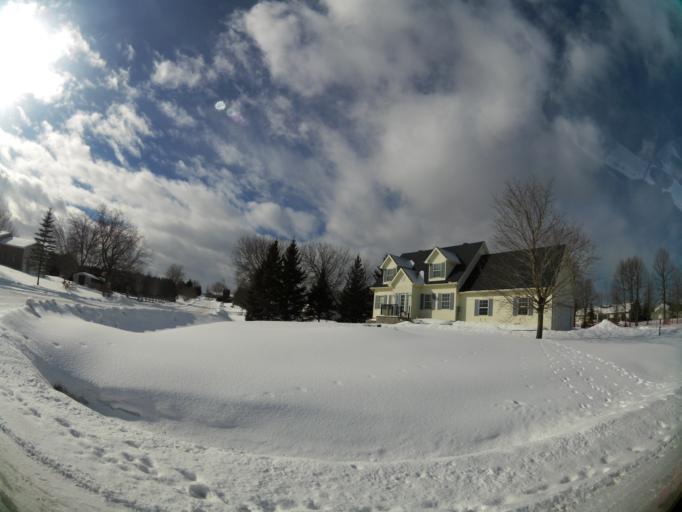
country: CA
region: Ontario
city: Ottawa
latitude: 45.2312
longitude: -75.4621
